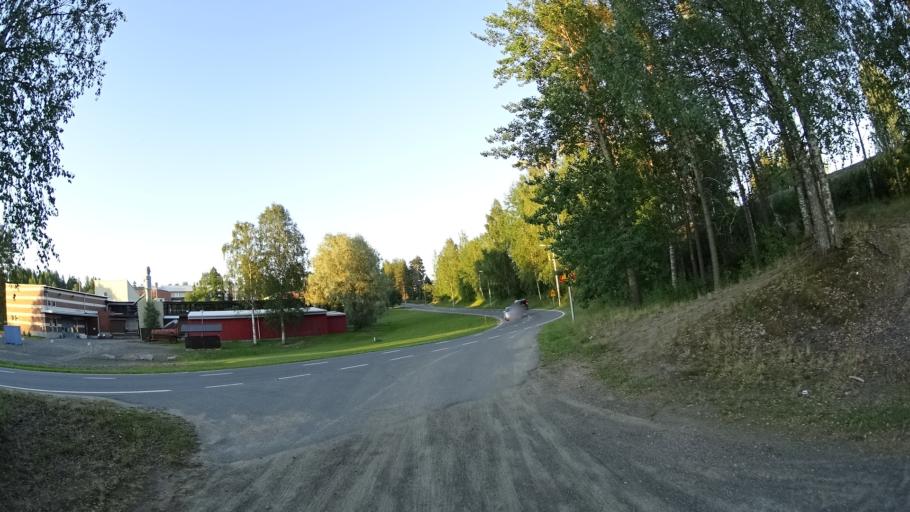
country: FI
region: Central Finland
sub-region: Jyvaeskylae
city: Petaejaevesi
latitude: 62.2564
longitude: 25.1783
